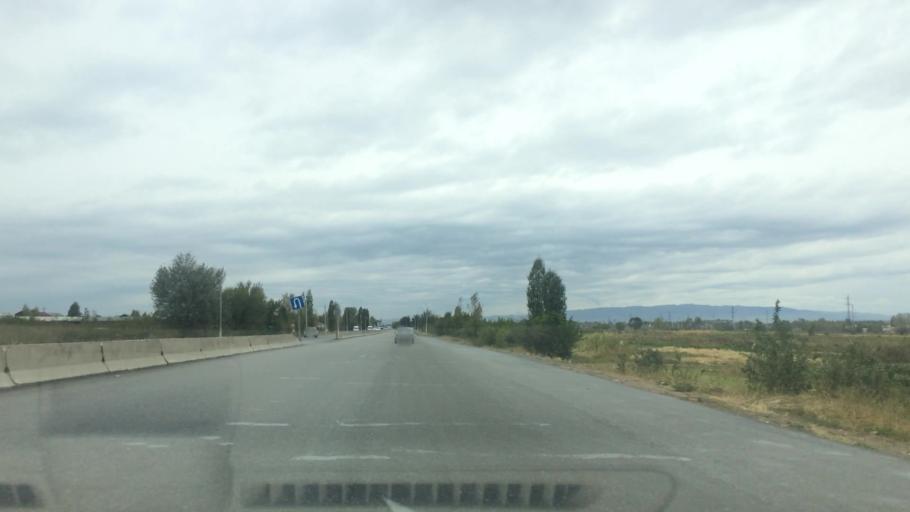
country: UZ
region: Jizzax
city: Jizzax
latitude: 40.0202
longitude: 67.6122
